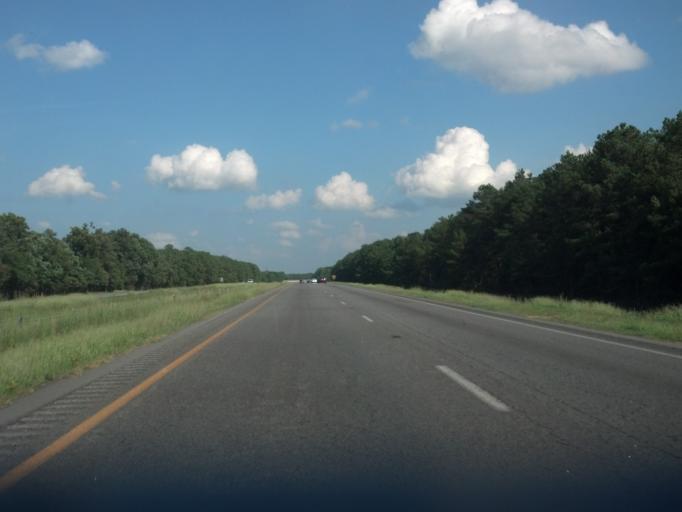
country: US
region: North Carolina
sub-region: Nash County
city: Rocky Mount
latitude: 35.9286
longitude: -77.6899
